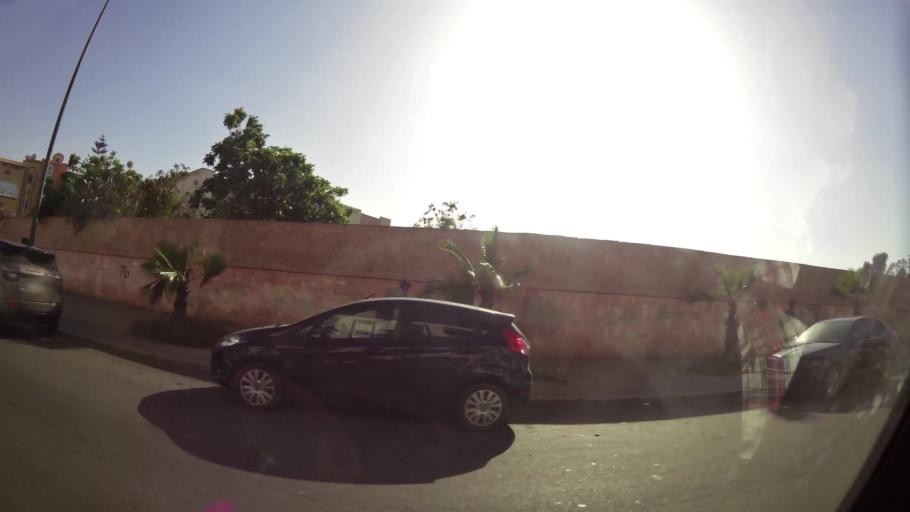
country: MA
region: Souss-Massa-Draa
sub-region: Inezgane-Ait Mellou
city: Inezgane
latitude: 30.3643
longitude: -9.5272
